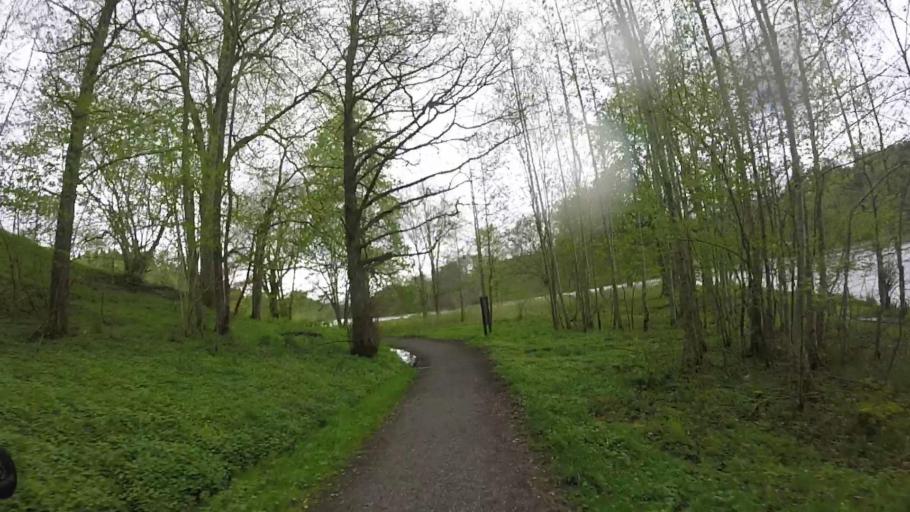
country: SE
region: Vaestra Goetaland
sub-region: Trollhattan
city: Trollhattan
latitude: 58.2696
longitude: 12.2573
